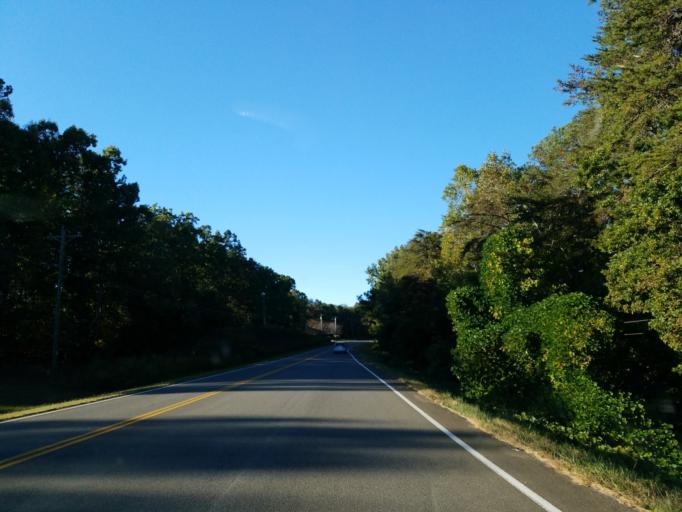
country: US
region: Georgia
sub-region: Pickens County
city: Nelson
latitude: 34.3935
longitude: -84.3804
